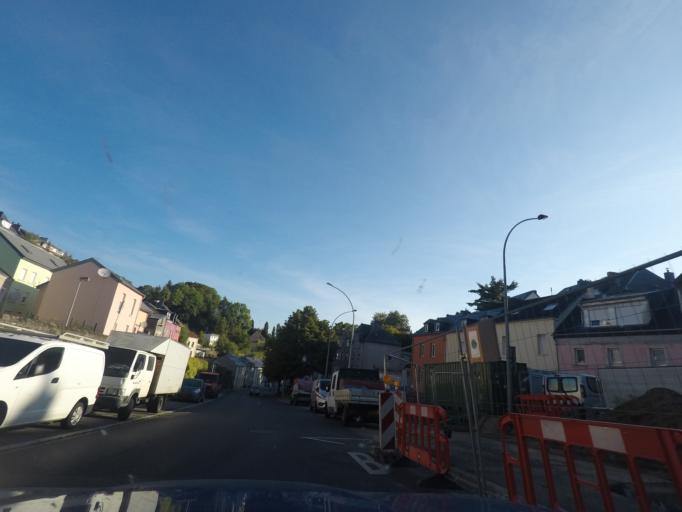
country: LU
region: Luxembourg
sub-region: Canton de Luxembourg
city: Luxembourg
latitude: 49.5991
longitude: 6.1426
